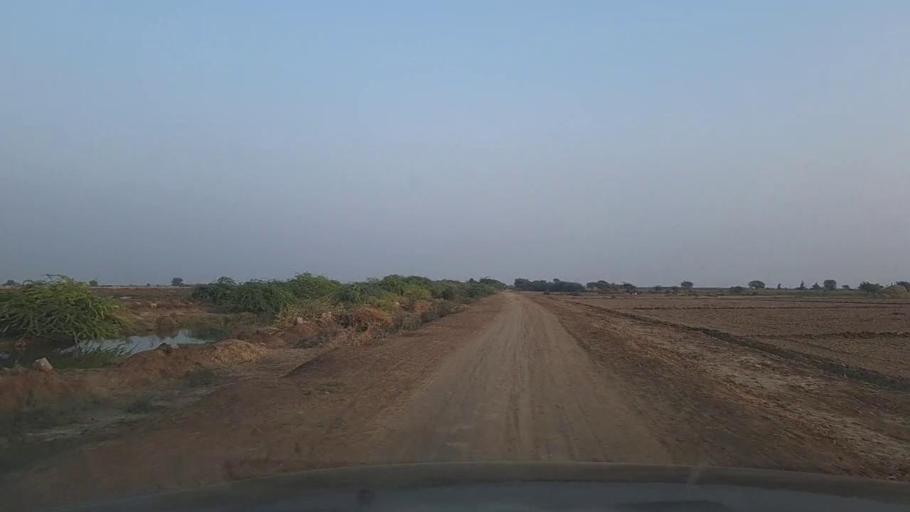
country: PK
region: Sindh
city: Jati
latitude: 24.5403
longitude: 68.4005
